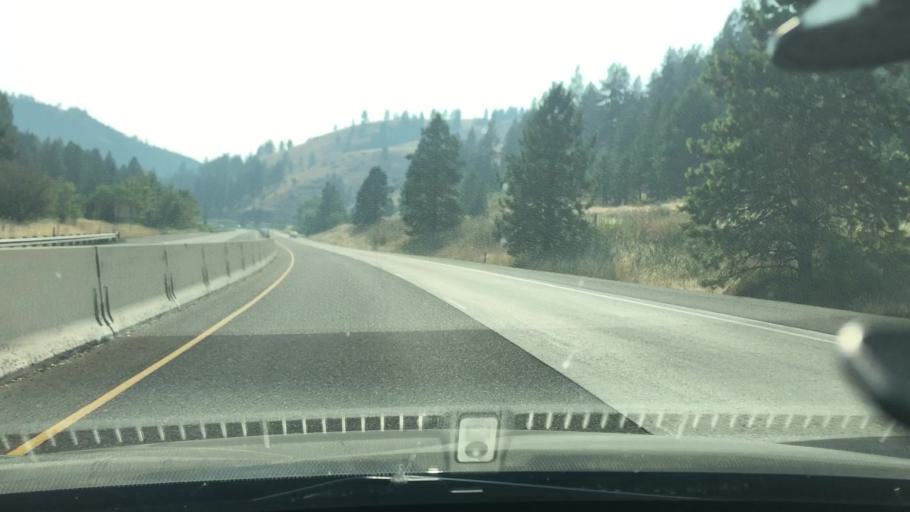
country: US
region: Oregon
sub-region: Union County
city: La Grande
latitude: 45.3547
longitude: -118.1896
